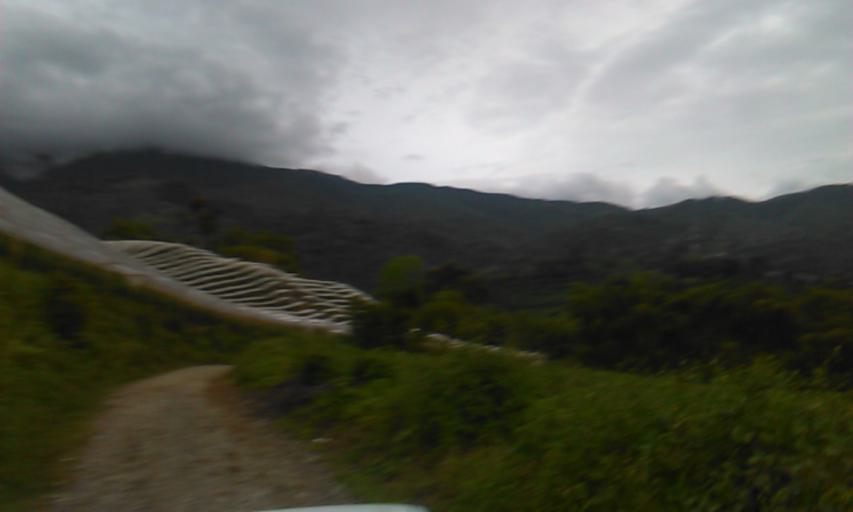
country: CO
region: Quindio
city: Cordoba
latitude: 4.4061
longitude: -75.6893
